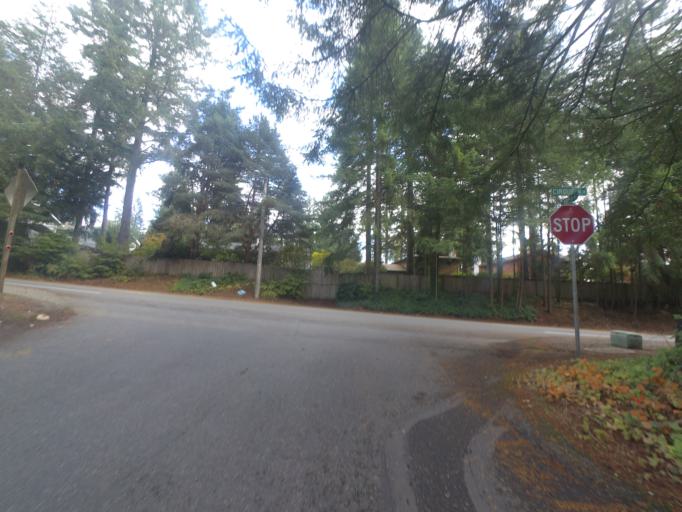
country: US
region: Washington
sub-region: Pierce County
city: University Place
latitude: 47.2122
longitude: -122.5604
